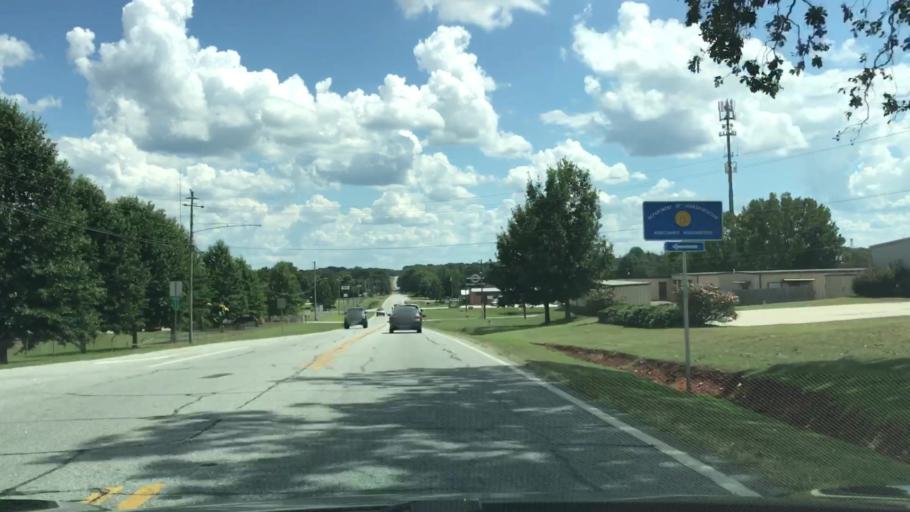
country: US
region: Georgia
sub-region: Oconee County
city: Watkinsville
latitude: 33.8563
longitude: -83.4024
